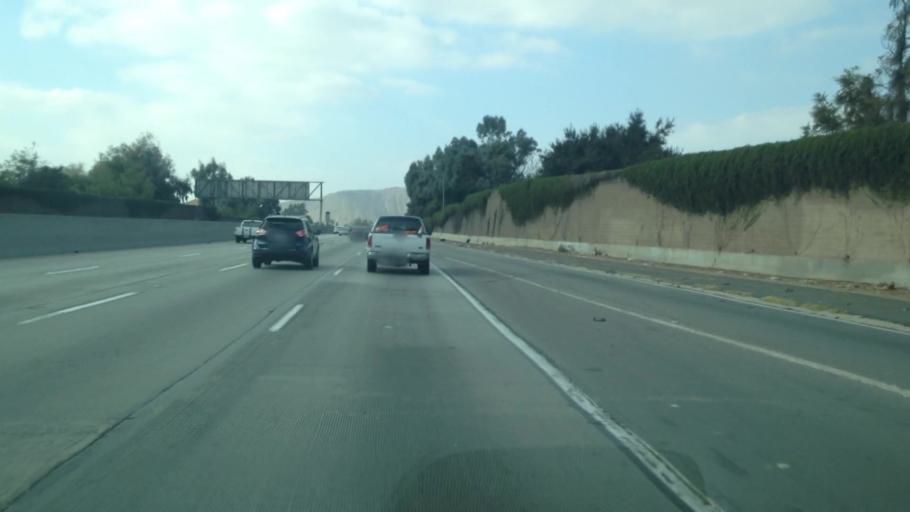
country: US
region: California
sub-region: Riverside County
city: Highgrove
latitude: 33.9975
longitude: -117.3669
